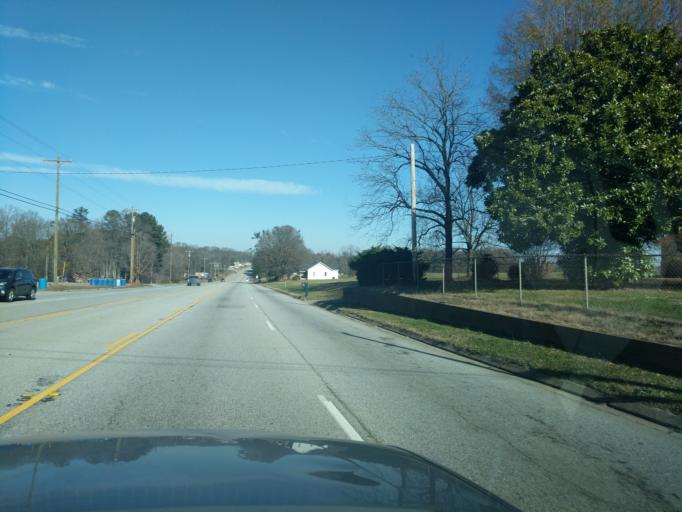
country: US
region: South Carolina
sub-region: Spartanburg County
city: Mayo
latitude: 35.0312
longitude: -81.8962
